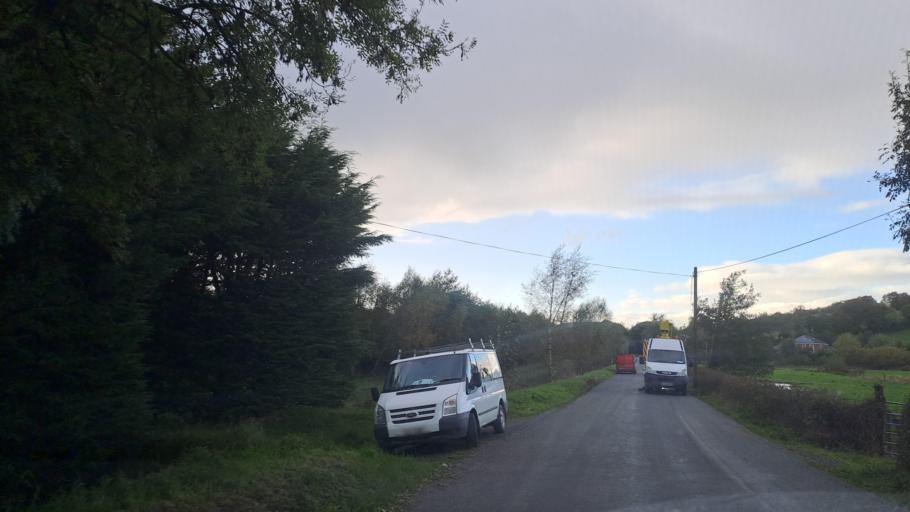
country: IE
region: Ulster
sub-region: County Monaghan
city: Castleblayney
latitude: 54.0394
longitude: -6.8266
